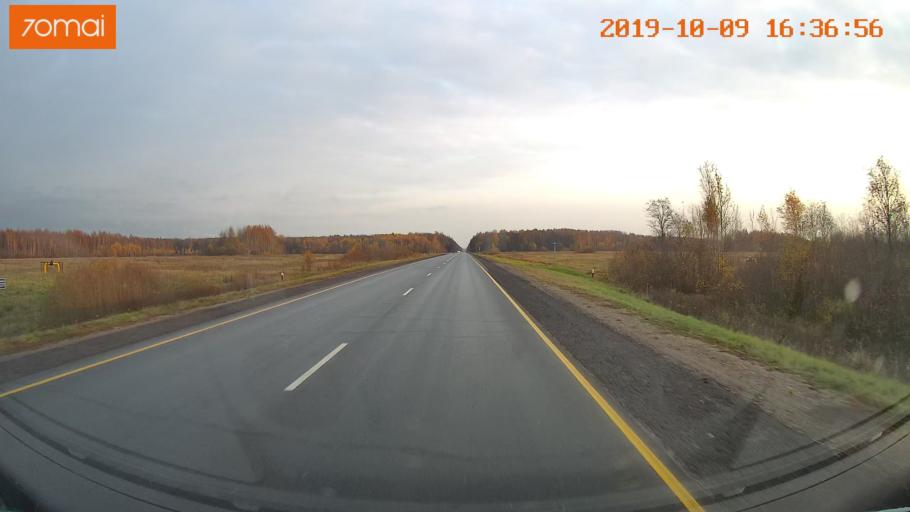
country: RU
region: Kostroma
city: Volgorechensk
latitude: 57.5345
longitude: 41.0184
